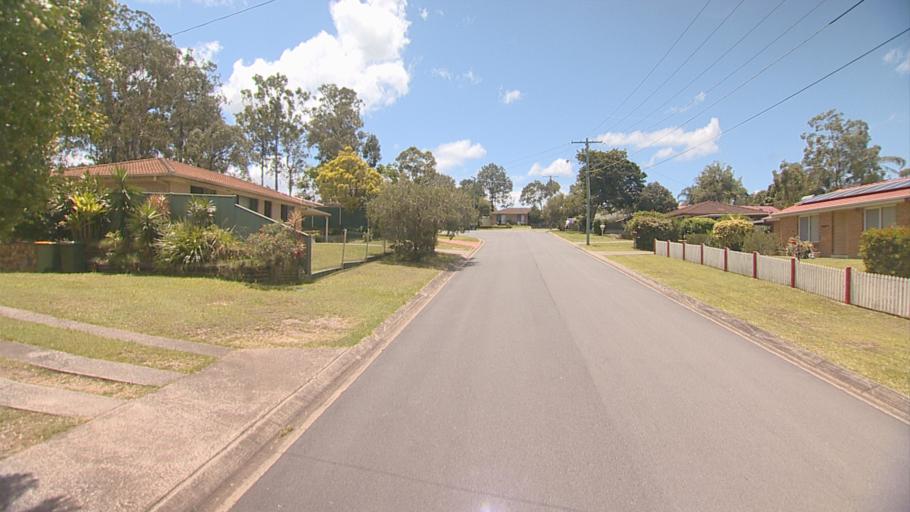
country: AU
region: Queensland
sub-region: Gold Coast
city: Yatala
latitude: -27.6977
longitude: 153.2169
